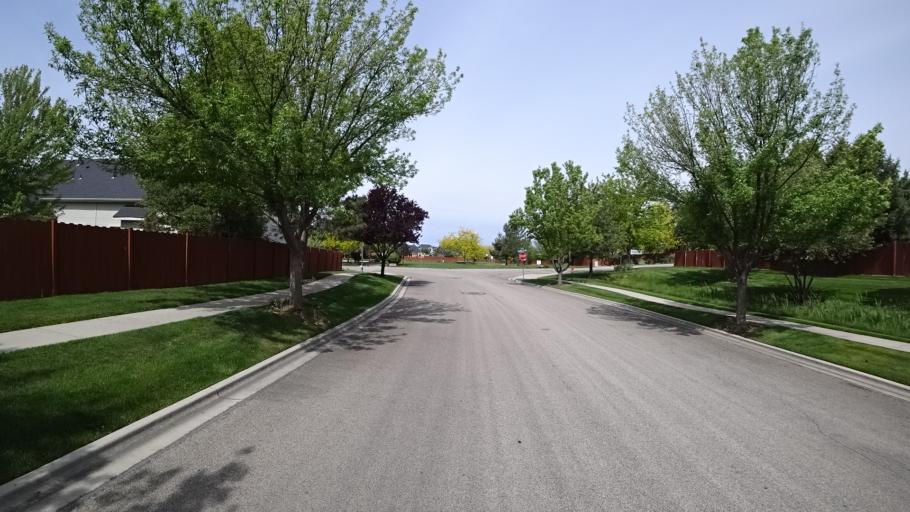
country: US
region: Idaho
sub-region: Ada County
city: Meridian
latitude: 43.5531
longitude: -116.3373
